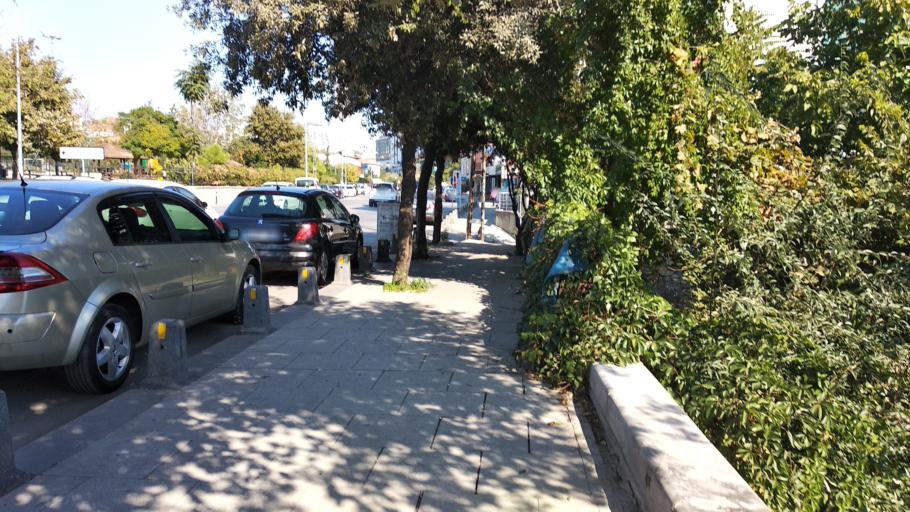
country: TR
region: Istanbul
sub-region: Atasehir
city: Atasehir
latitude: 40.9987
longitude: 29.0933
